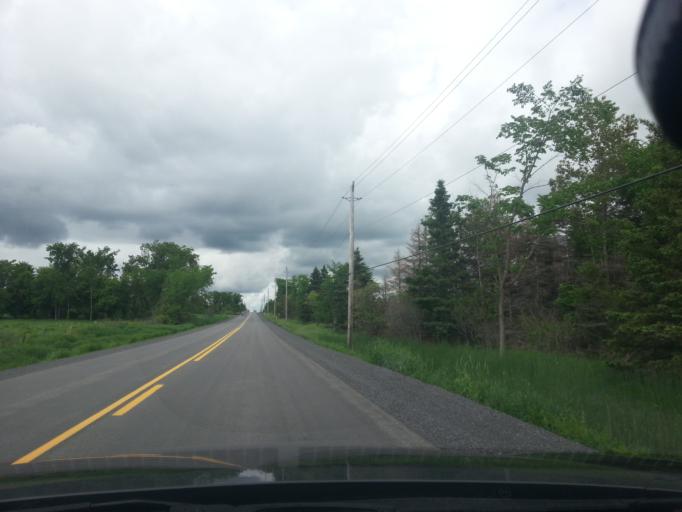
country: CA
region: Ontario
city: Carleton Place
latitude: 45.1788
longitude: -75.9971
